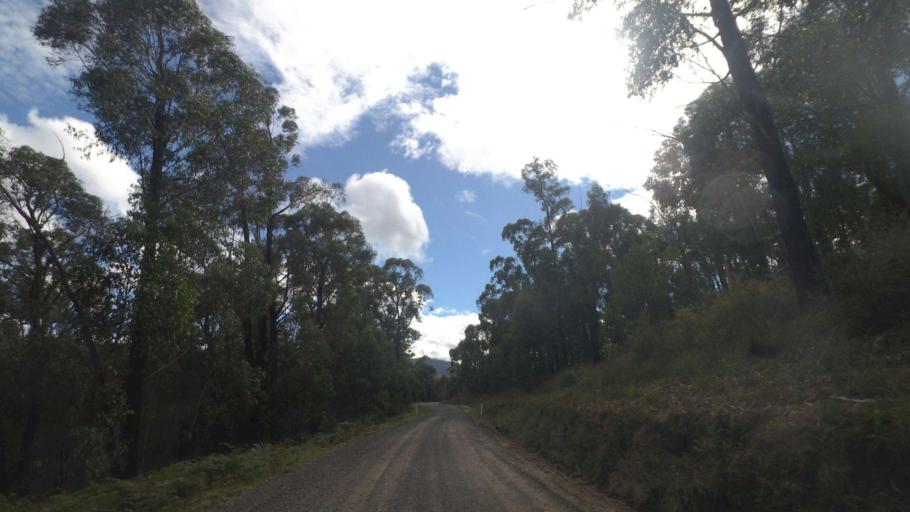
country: AU
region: Victoria
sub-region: Cardinia
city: Bunyip
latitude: -38.0035
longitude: 145.8066
